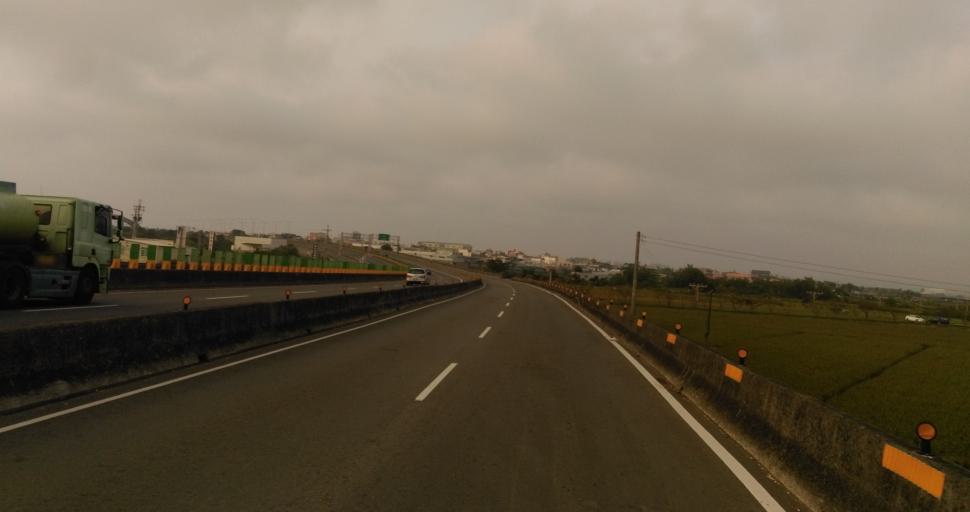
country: TW
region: Taiwan
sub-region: Hsinchu
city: Hsinchu
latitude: 24.7995
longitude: 120.9206
